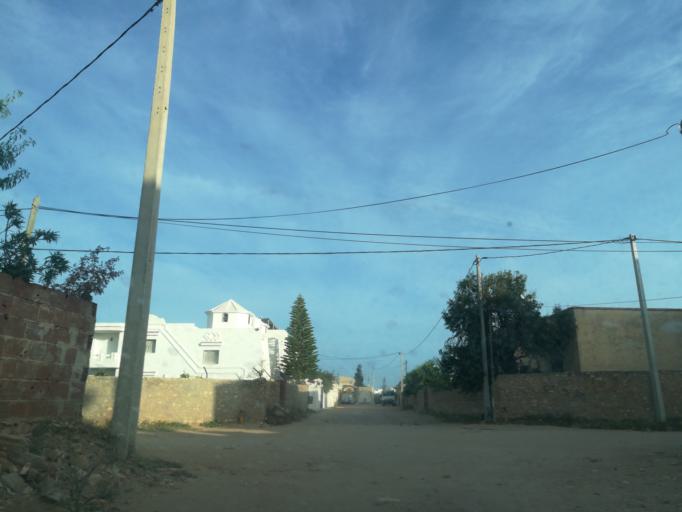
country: TN
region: Safaqis
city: Al Qarmadah
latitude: 34.8122
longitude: 10.7539
